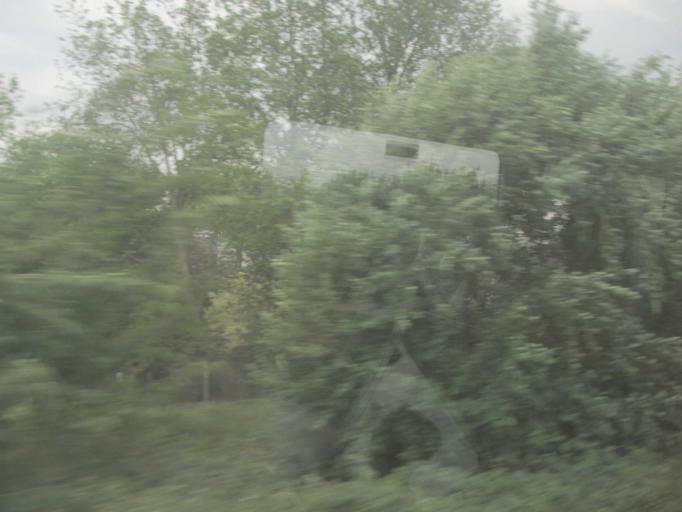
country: GB
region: England
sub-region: Greater London
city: Hendon
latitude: 51.5957
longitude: -0.2367
